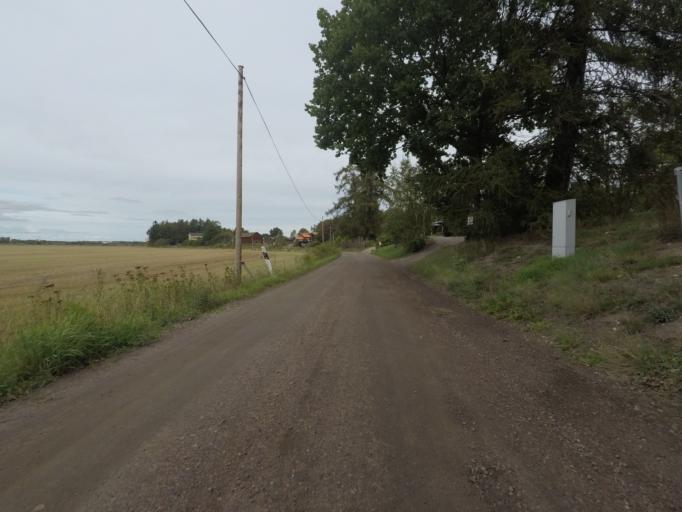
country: SE
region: Vaestmanland
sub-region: Kungsors Kommun
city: Kungsoer
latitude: 59.4551
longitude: 16.0751
